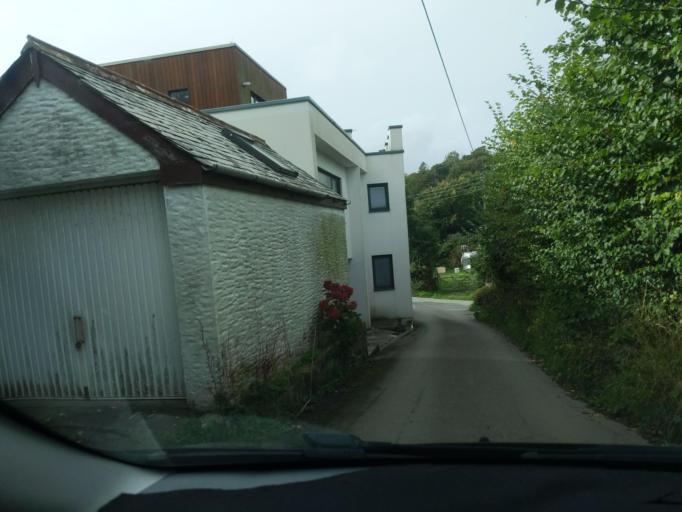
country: GB
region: England
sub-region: Cornwall
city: Mevagissey
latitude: 50.2394
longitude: -4.7915
